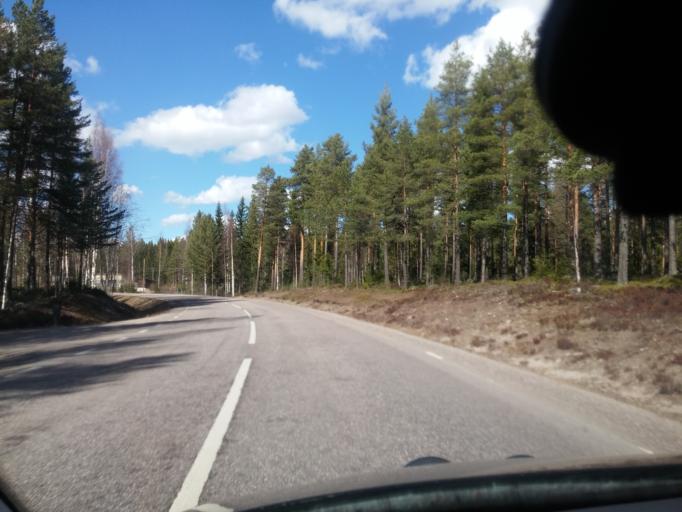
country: SE
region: Gaevleborg
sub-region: Ovanakers Kommun
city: Edsbyn
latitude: 61.2508
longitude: 15.8934
